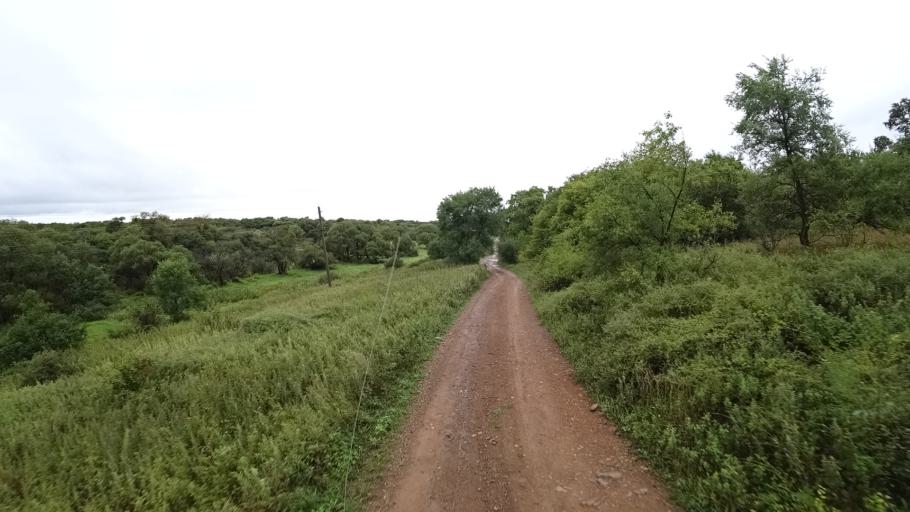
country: RU
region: Primorskiy
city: Monastyrishche
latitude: 44.2687
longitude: 132.4039
